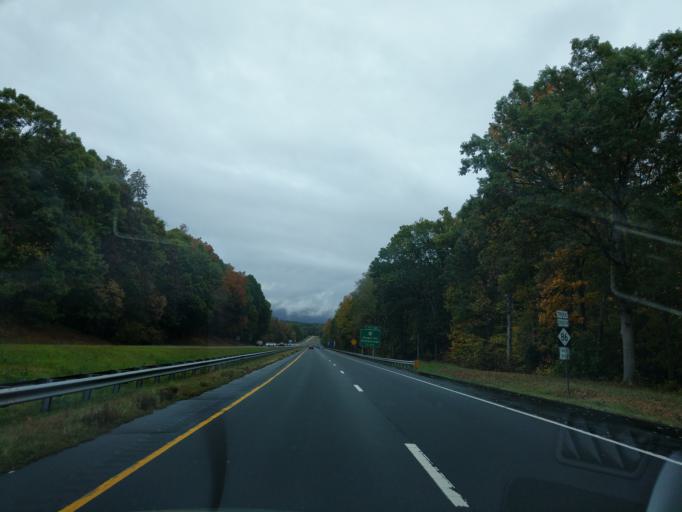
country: US
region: North Carolina
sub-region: Orange County
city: Hillsborough
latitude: 36.0558
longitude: -79.0962
